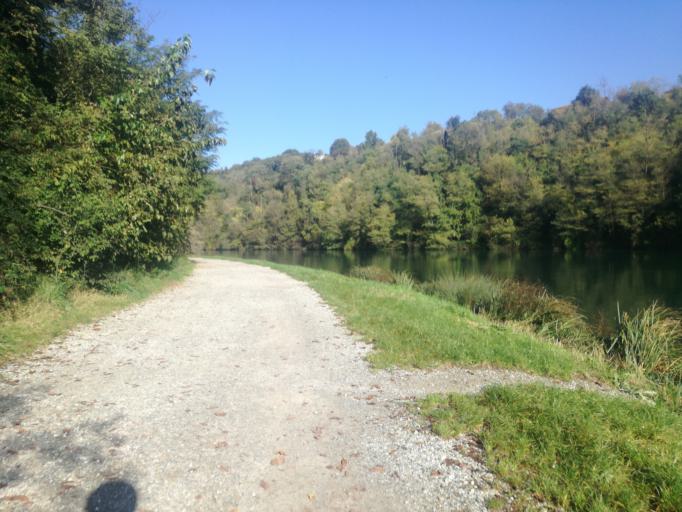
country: IT
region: Lombardy
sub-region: Provincia di Bergamo
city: Capriate San Gervasio
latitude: 45.6229
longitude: 9.5170
